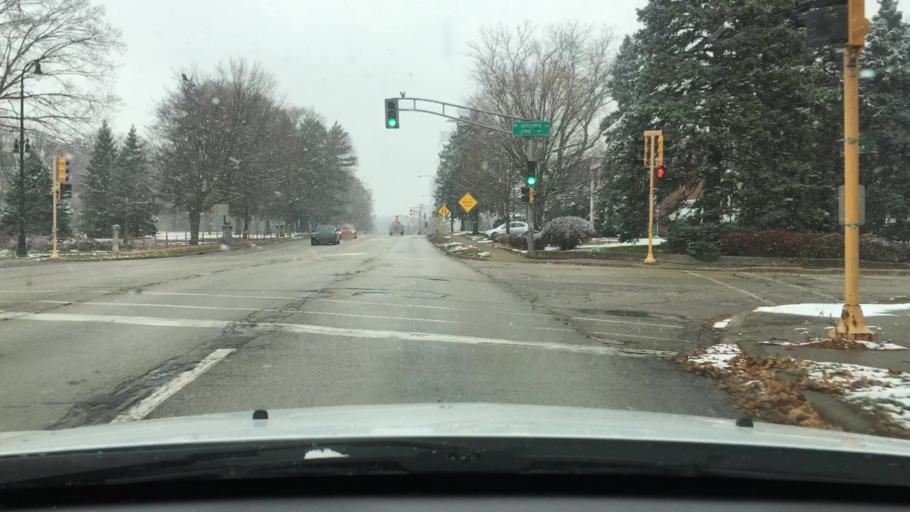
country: US
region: Illinois
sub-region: DeKalb County
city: DeKalb
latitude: 41.9337
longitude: -88.7525
